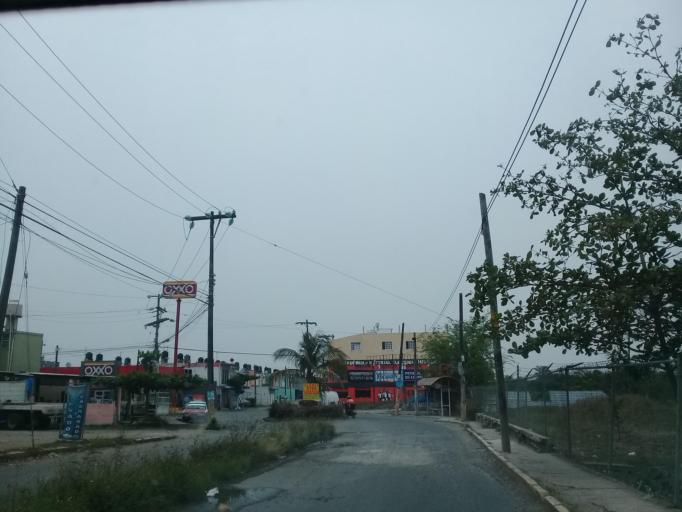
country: MX
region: Veracruz
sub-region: Veracruz
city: Las Amapolas
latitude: 19.1583
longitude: -96.2075
